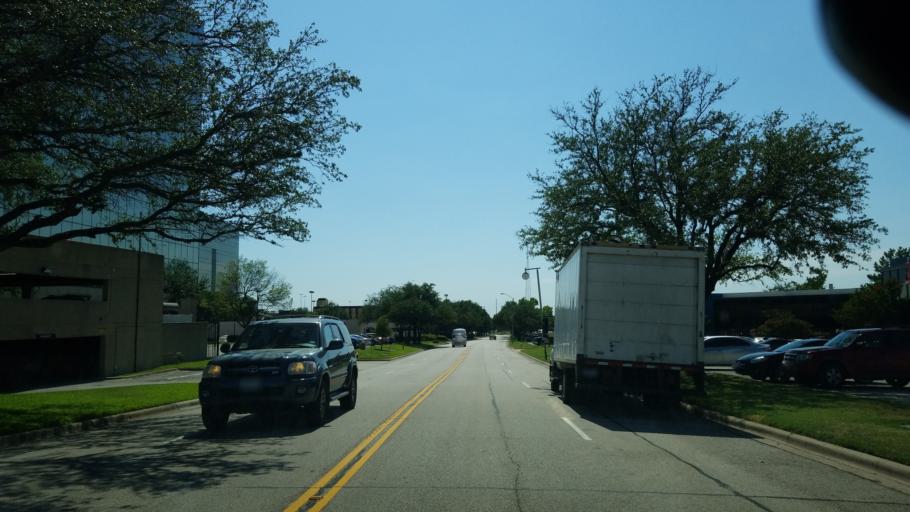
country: US
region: Texas
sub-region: Dallas County
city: Farmers Branch
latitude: 32.9118
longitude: -96.8852
